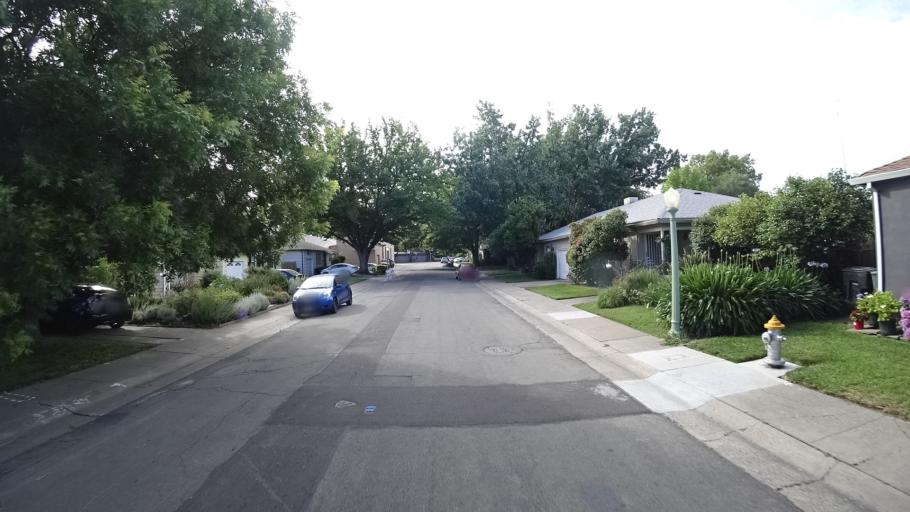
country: US
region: California
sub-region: Sacramento County
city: Sacramento
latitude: 38.5597
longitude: -121.5059
